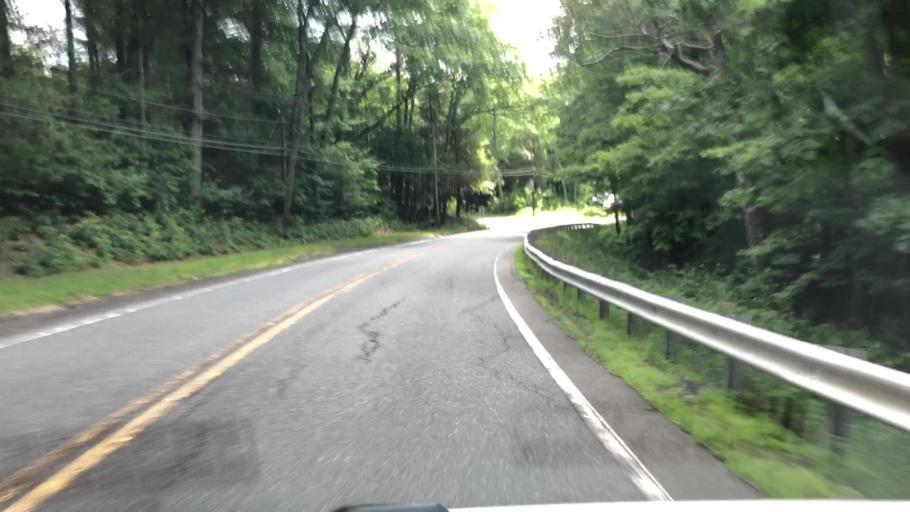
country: US
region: Massachusetts
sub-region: Hampshire County
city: Williamsburg
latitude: 42.4254
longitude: -72.7808
